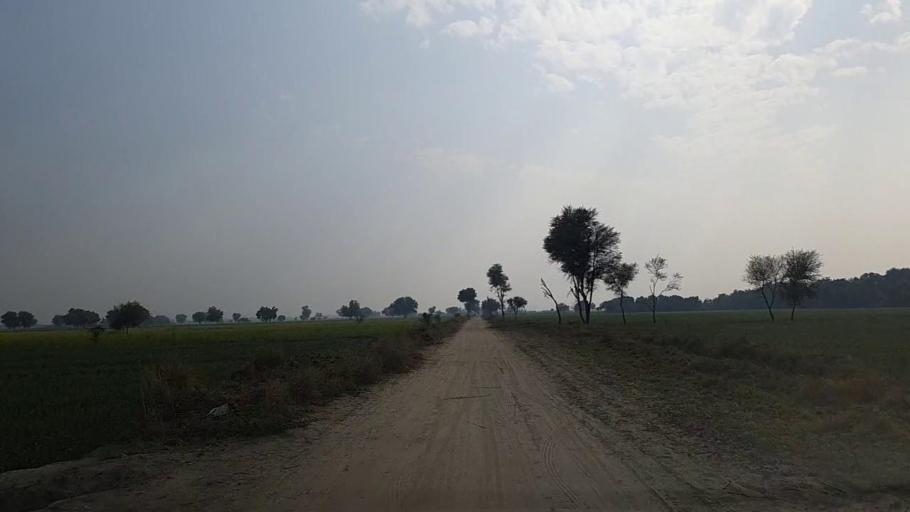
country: PK
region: Sindh
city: Nawabshah
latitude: 26.2866
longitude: 68.4458
